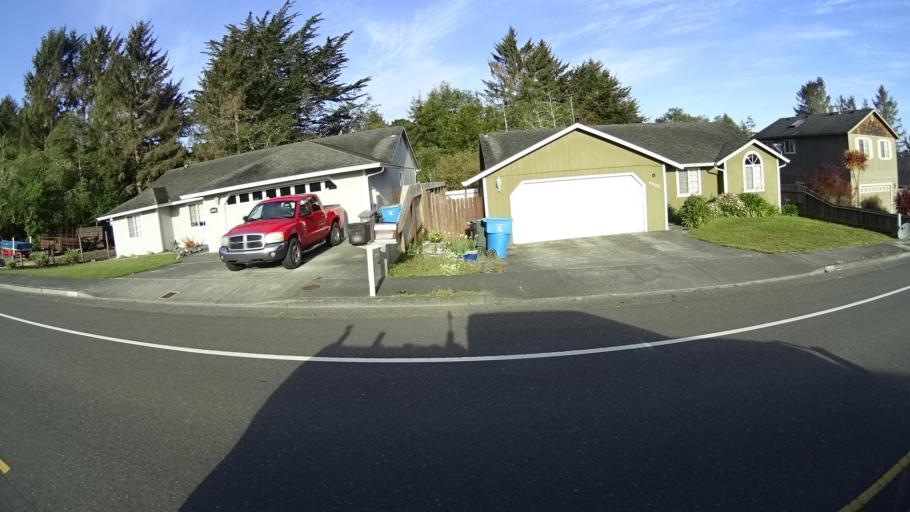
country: US
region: California
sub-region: Humboldt County
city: Humboldt Hill
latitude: 40.7304
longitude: -124.2021
